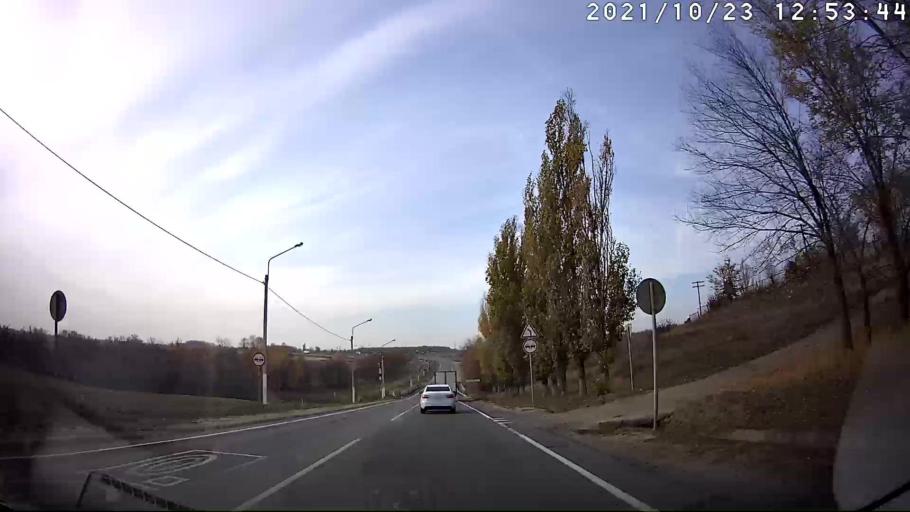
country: RU
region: Volgograd
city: Dubovka
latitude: 49.0573
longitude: 44.8098
